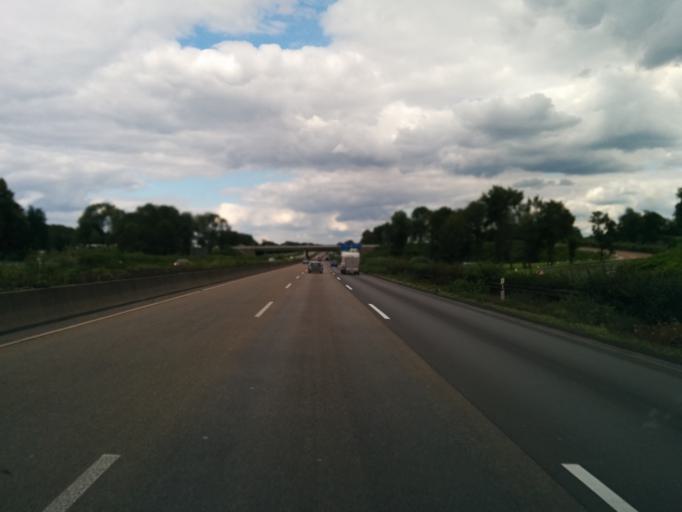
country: DE
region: North Rhine-Westphalia
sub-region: Regierungsbezirk Dusseldorf
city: Duisburg
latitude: 51.4455
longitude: 6.7739
